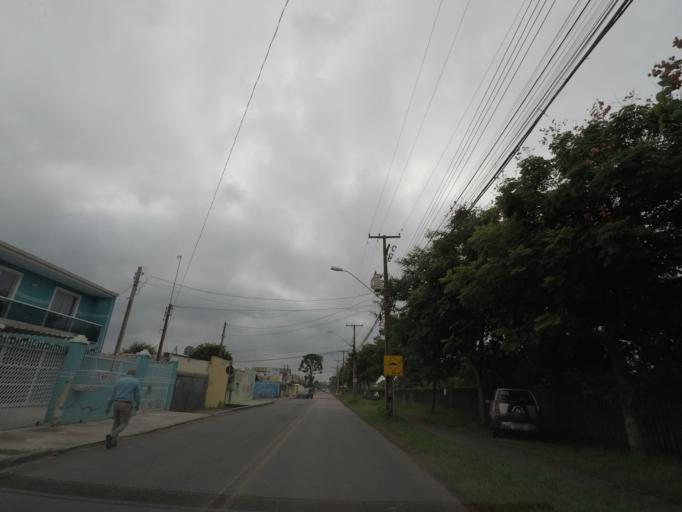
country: BR
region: Parana
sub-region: Curitiba
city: Curitiba
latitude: -25.5026
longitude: -49.3348
